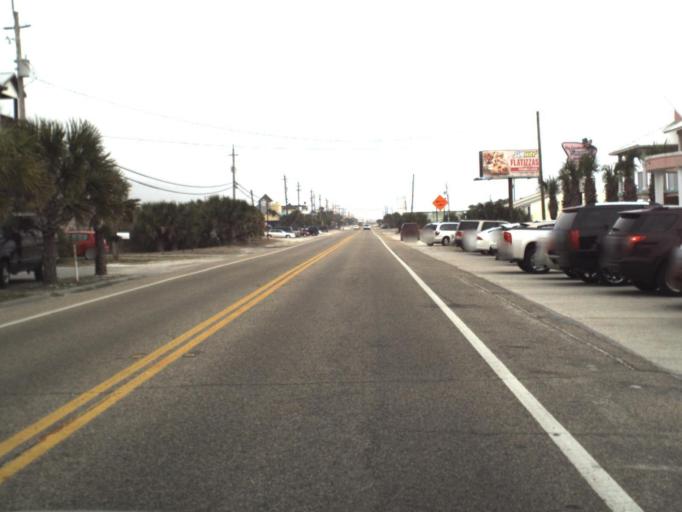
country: US
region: Florida
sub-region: Bay County
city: Laguna Beach
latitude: 30.2431
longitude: -85.9323
